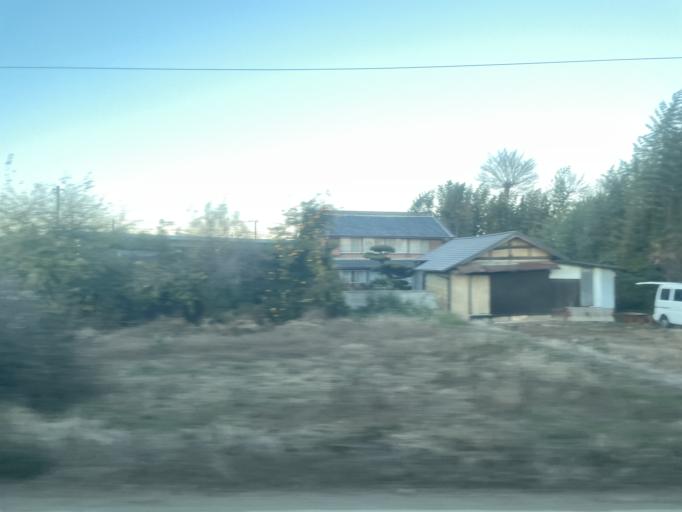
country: JP
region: Saitama
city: Honjo
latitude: 36.2082
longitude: 139.2323
